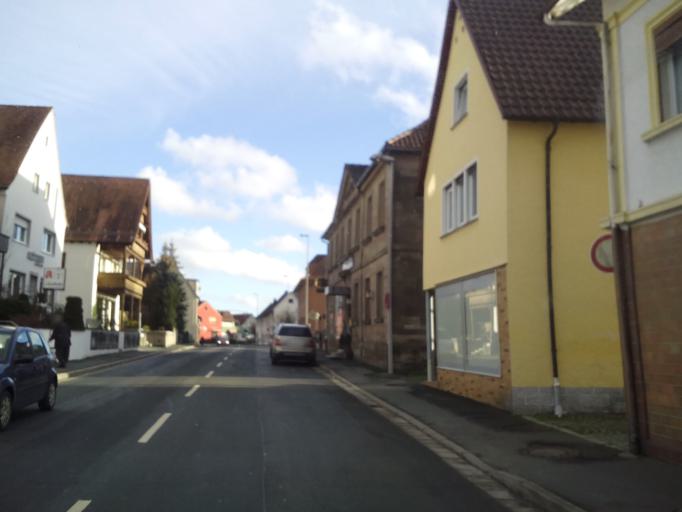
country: DE
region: Bavaria
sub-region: Upper Franconia
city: Mainleus
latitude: 50.1000
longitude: 11.3753
